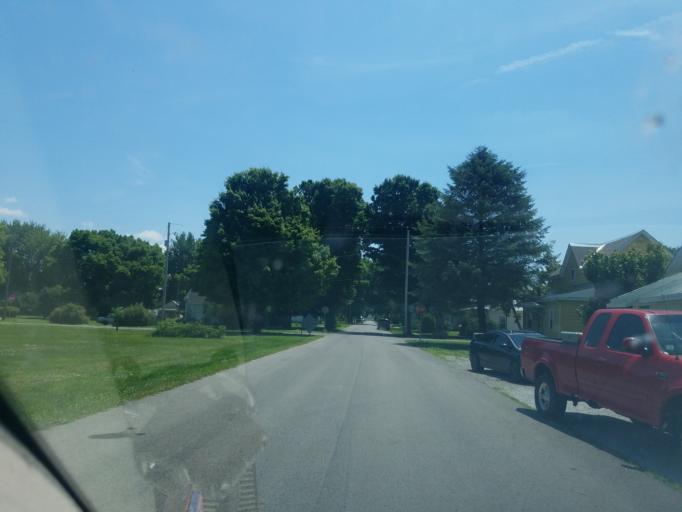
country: US
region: Ohio
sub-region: Hardin County
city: Kenton
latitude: 40.6416
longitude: -83.6168
